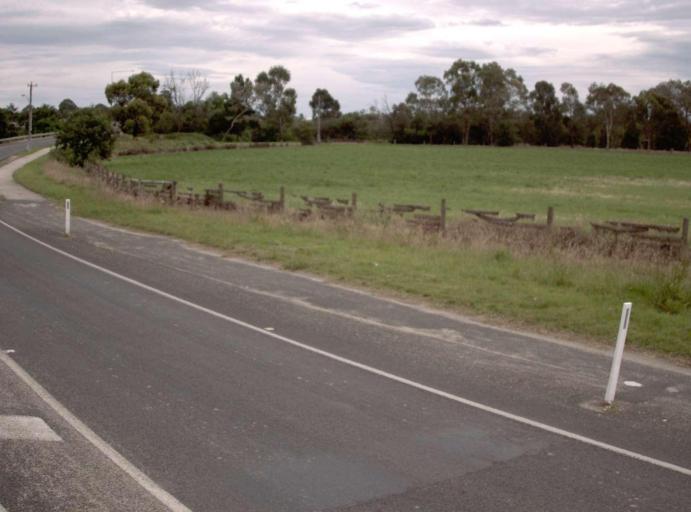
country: AU
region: Victoria
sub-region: East Gippsland
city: Bairnsdale
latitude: -37.8162
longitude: 147.6173
